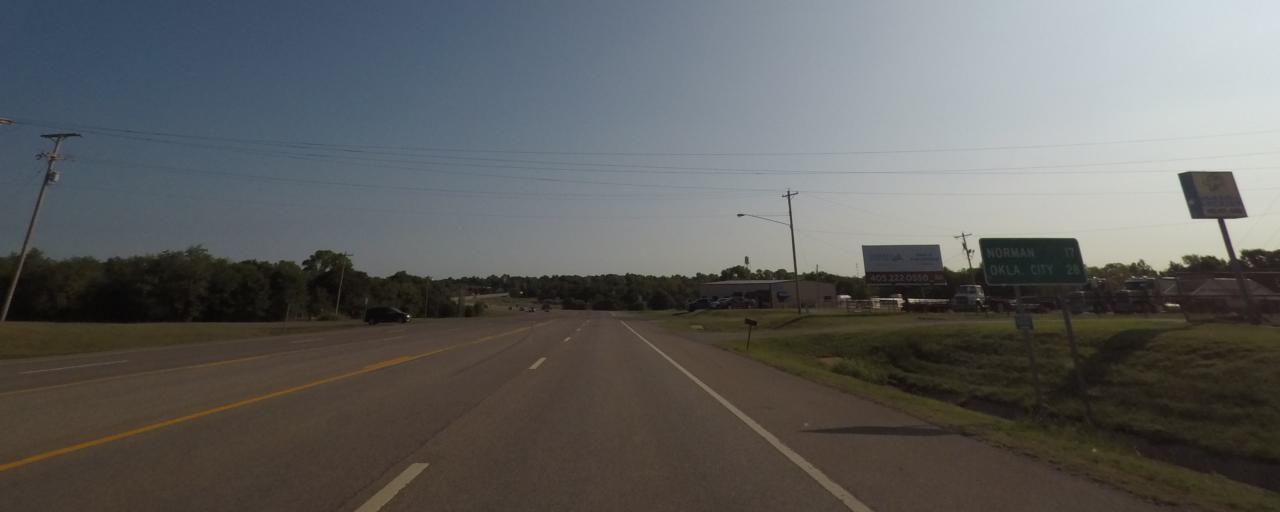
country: US
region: Oklahoma
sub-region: McClain County
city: Blanchard
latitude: 35.1307
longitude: -97.6670
